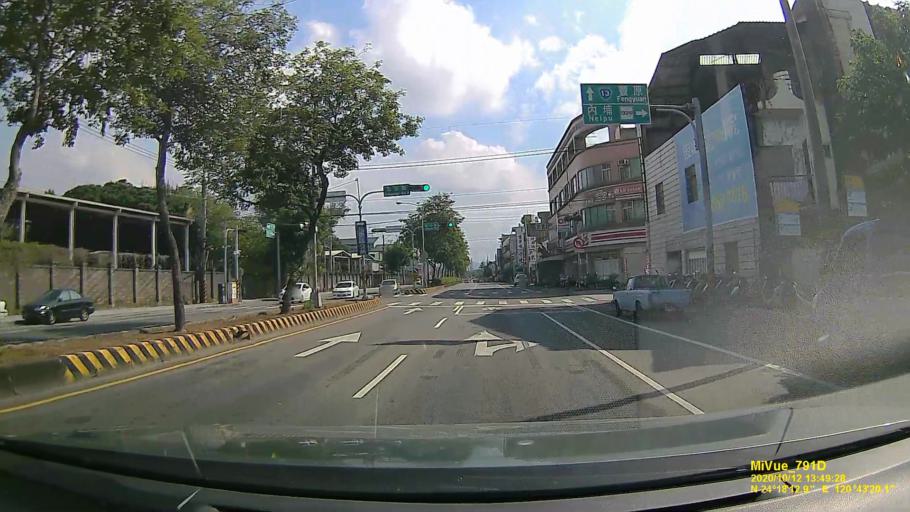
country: TW
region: Taiwan
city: Fengyuan
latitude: 24.3037
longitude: 120.7222
